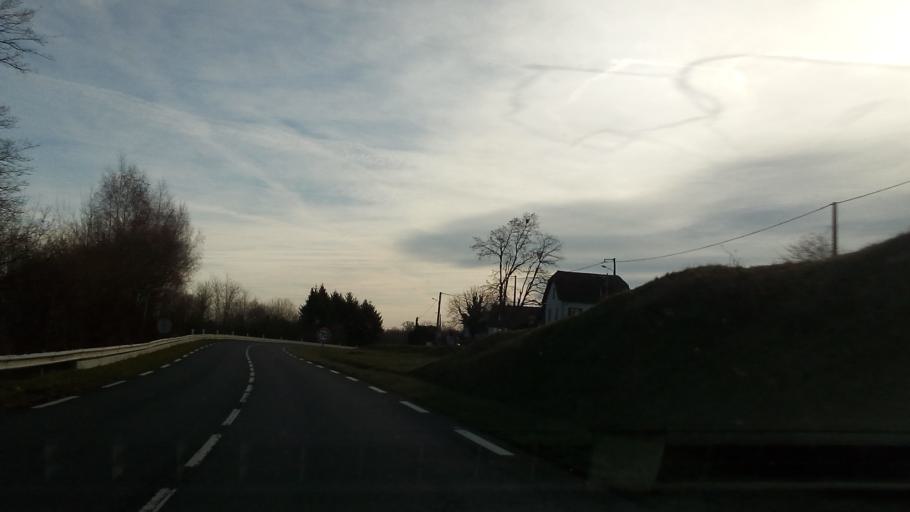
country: FR
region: Limousin
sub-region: Departement de la Correze
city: Seilhac
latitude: 45.3450
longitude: 1.7435
